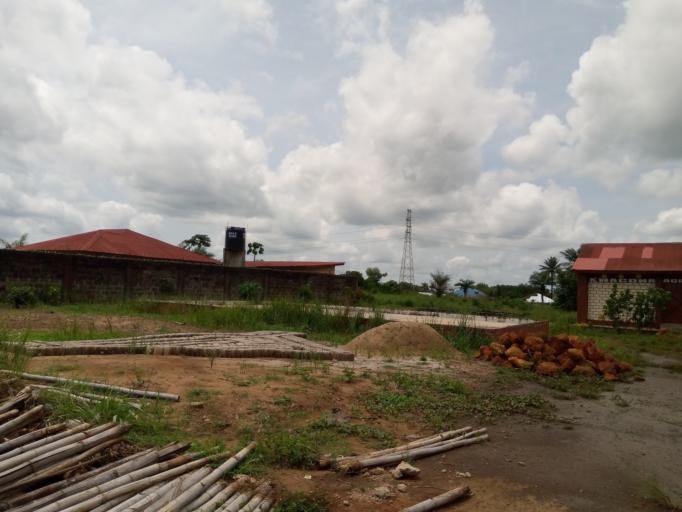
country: SL
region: Western Area
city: Waterloo
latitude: 8.3592
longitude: -12.9691
